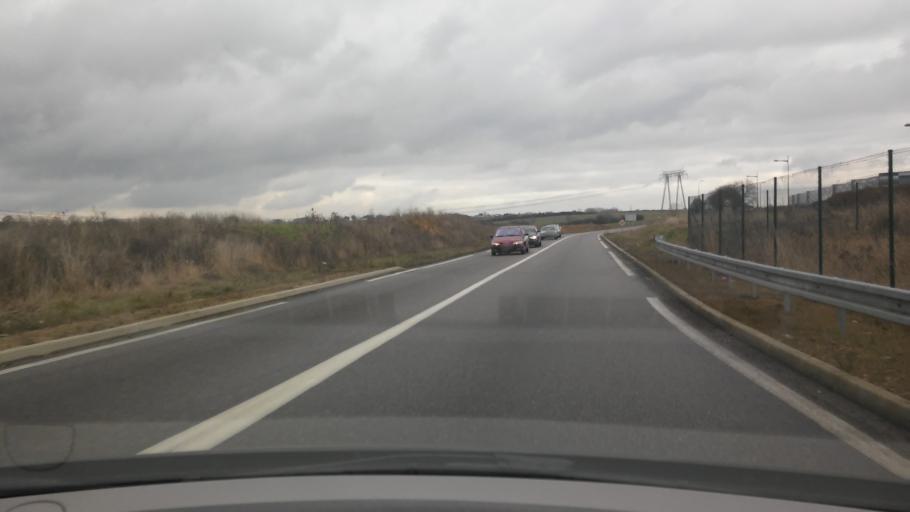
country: FR
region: Lorraine
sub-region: Departement de la Moselle
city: Retonfey
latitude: 49.1173
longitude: 6.2778
